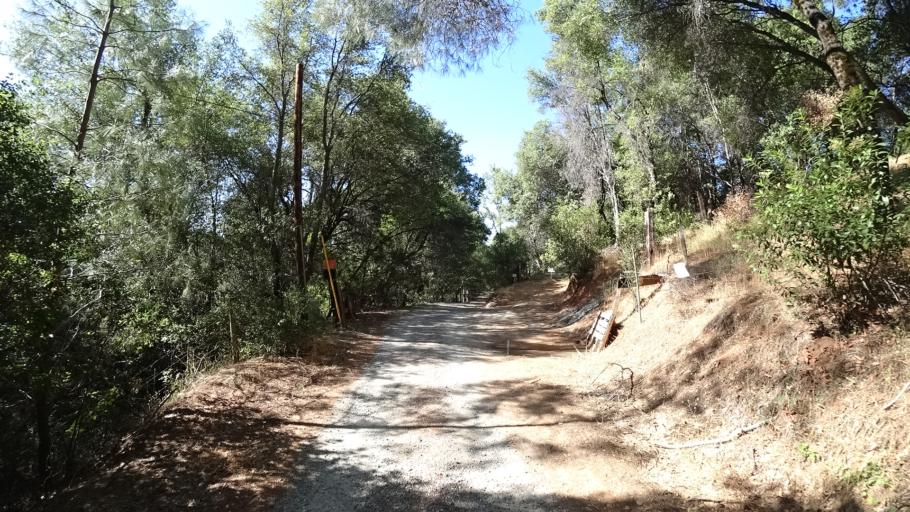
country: US
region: California
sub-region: Amador County
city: Pioneer
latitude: 38.3931
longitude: -120.5711
